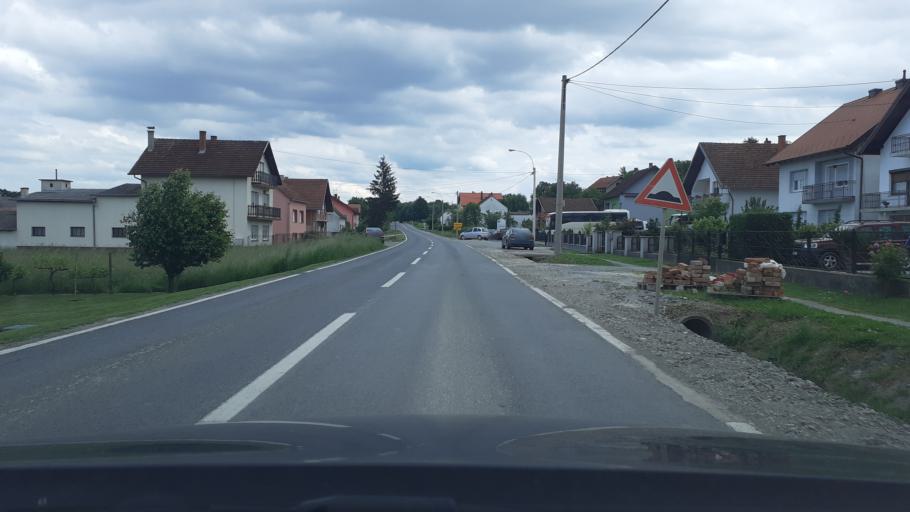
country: HR
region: Pozesko-Slavonska
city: Jaksic
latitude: 45.3241
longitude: 17.7617
